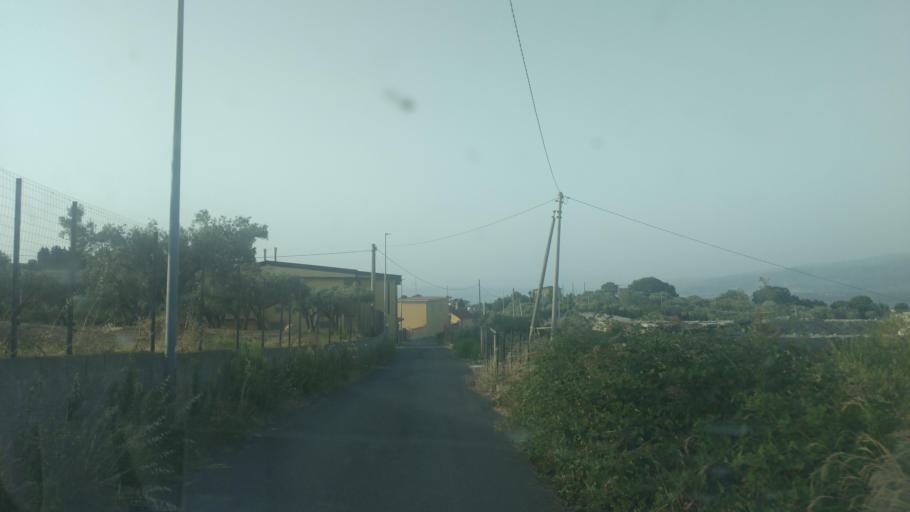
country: IT
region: Calabria
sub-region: Provincia di Catanzaro
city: Staletti
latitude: 38.7635
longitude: 16.5328
